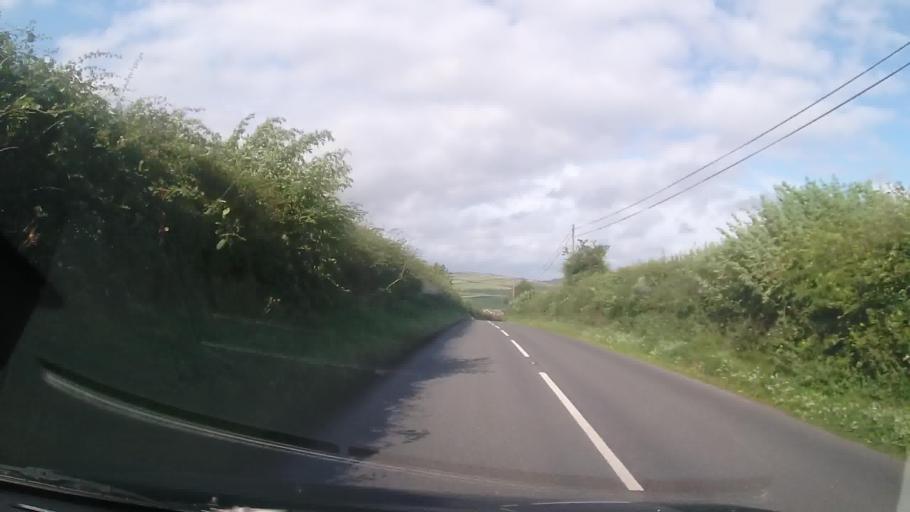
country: GB
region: Wales
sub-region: Sir Powys
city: Knighton
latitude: 52.3743
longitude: -3.0491
